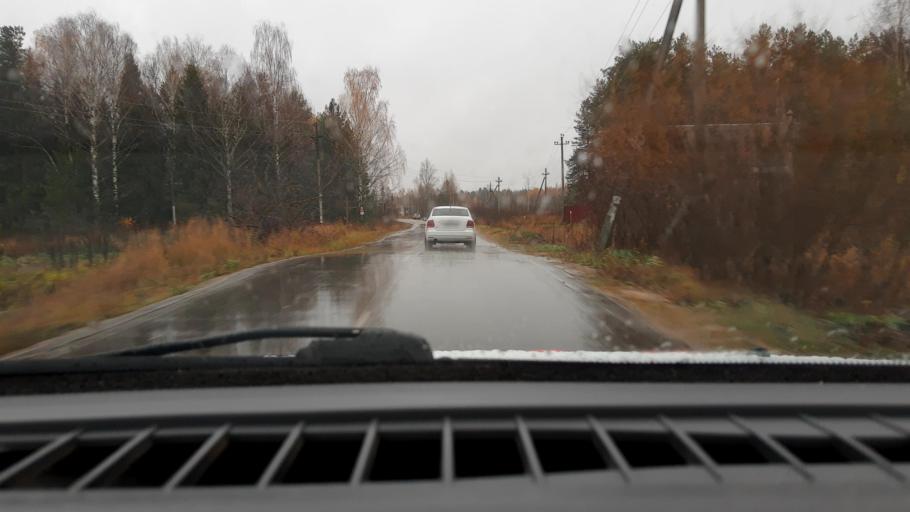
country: RU
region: Nizjnij Novgorod
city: Linda
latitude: 56.6797
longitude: 44.1958
